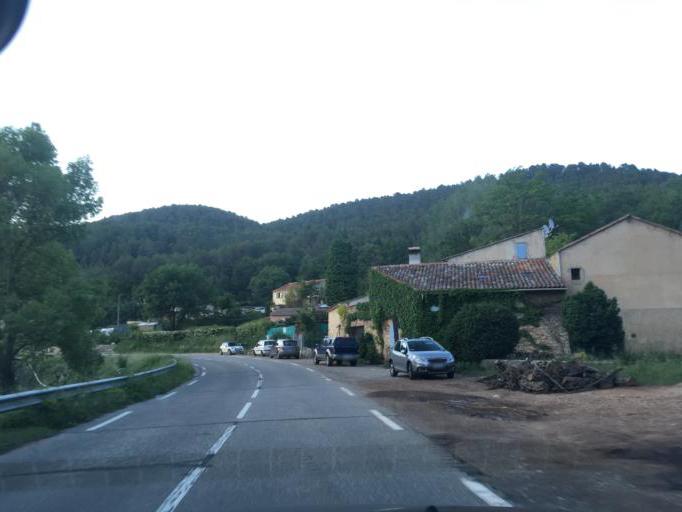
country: FR
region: Provence-Alpes-Cote d'Azur
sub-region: Departement du Var
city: Salernes
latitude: 43.5421
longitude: 6.2562
